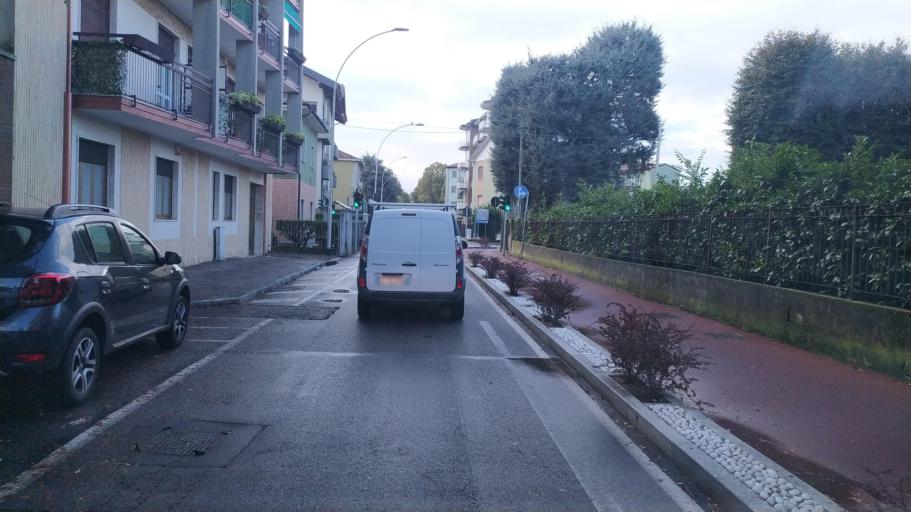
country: IT
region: Lombardy
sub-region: Citta metropolitana di Milano
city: Gaggiano
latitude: 45.4052
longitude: 9.0337
